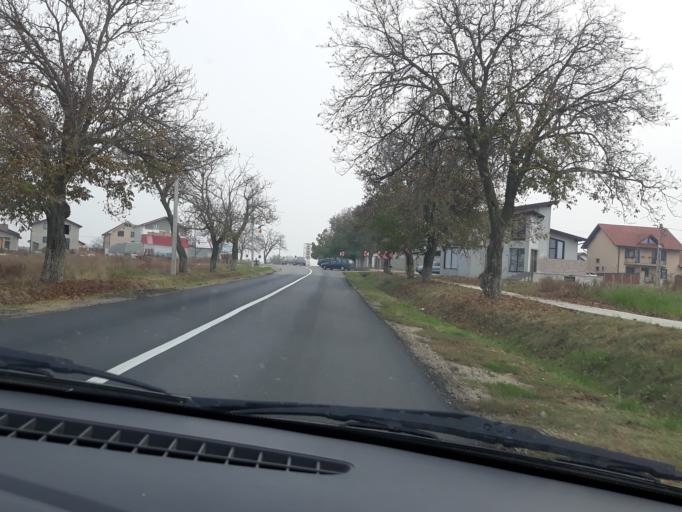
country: RO
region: Bihor
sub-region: Comuna Santandrei
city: Santandrei
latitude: 47.0556
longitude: 21.8677
